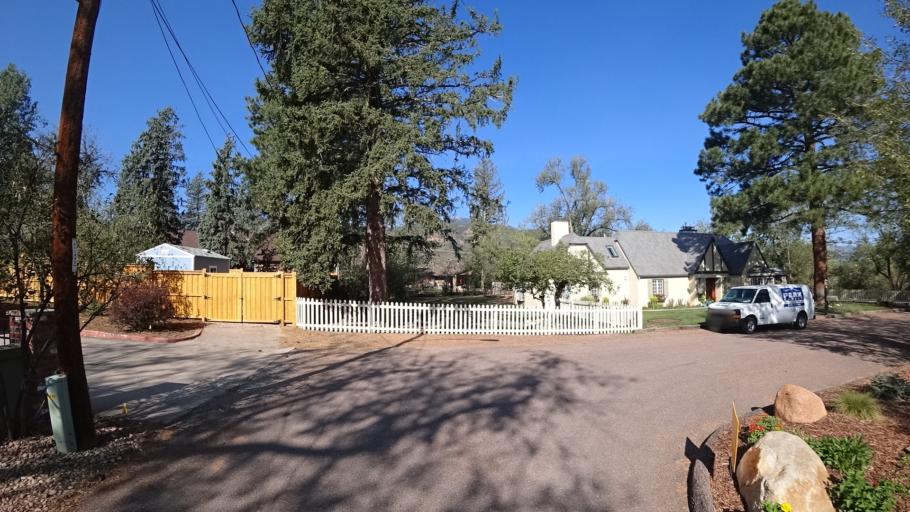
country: US
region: Colorado
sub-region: El Paso County
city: Colorado Springs
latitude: 38.7958
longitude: -104.8506
